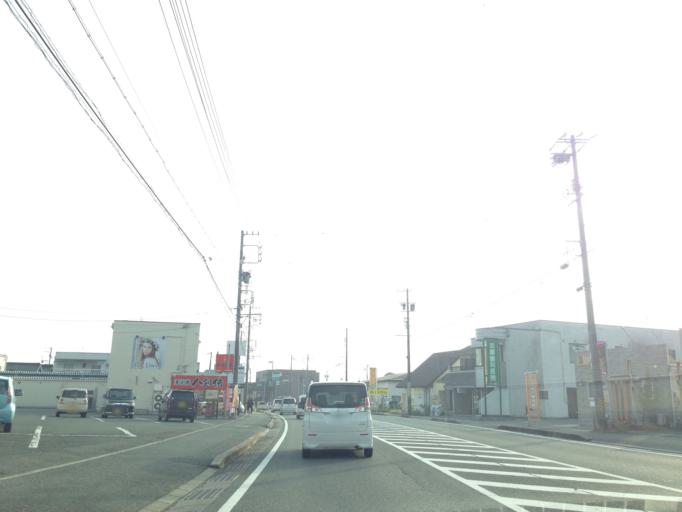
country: JP
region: Aichi
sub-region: Tokai-shi
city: Toyokawa
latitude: 34.8534
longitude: 137.4210
